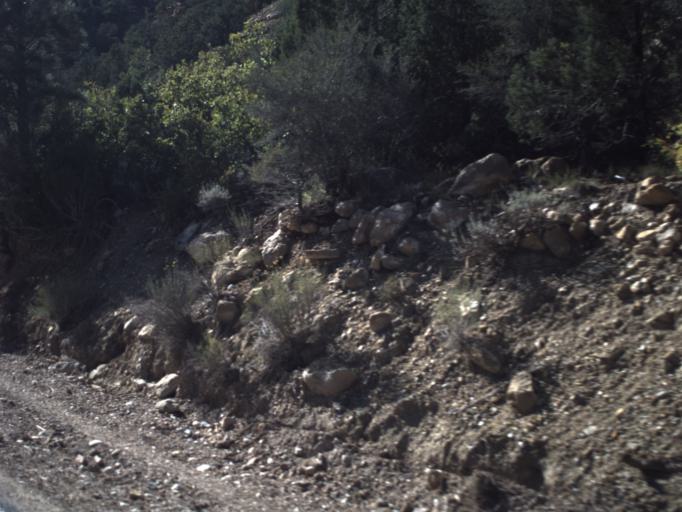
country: US
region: Utah
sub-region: Iron County
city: Parowan
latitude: 37.7804
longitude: -112.8329
